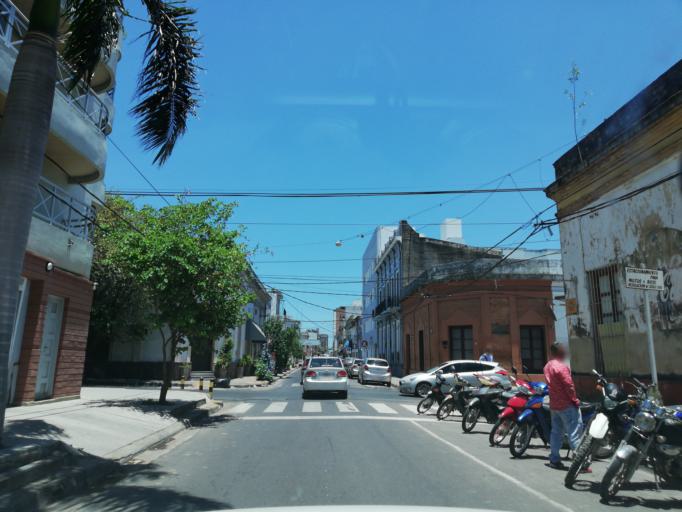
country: AR
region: Corrientes
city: Corrientes
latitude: -27.4620
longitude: -58.8337
